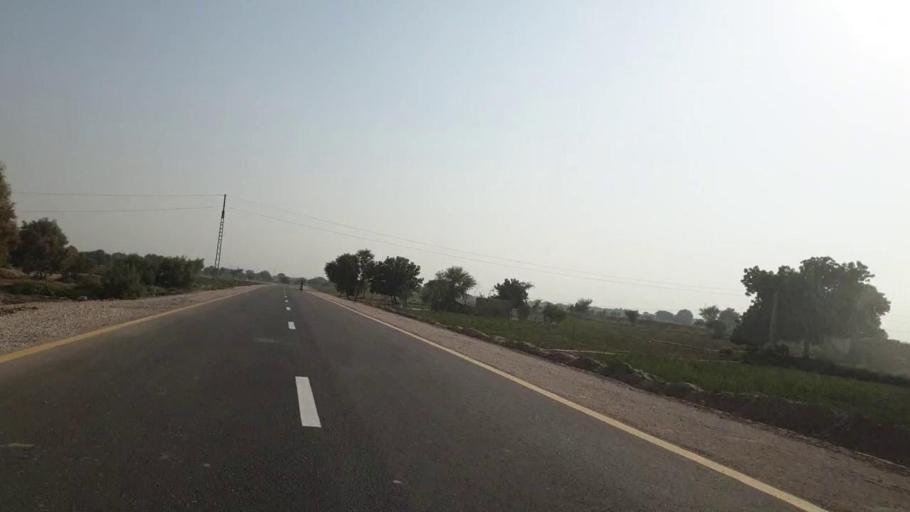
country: PK
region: Sindh
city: Bhan
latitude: 26.4861
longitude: 67.7795
